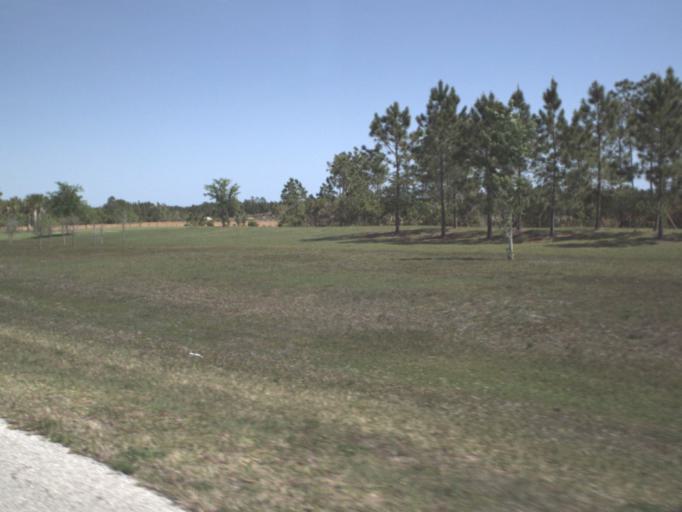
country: US
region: Florida
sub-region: Flagler County
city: Palm Coast
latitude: 29.5740
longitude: -81.2752
